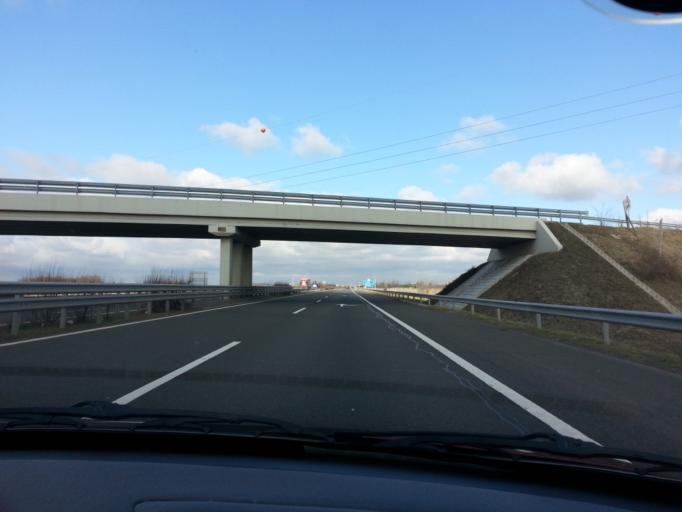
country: HU
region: Csongrad
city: Kistelek
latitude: 46.4549
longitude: 19.9325
